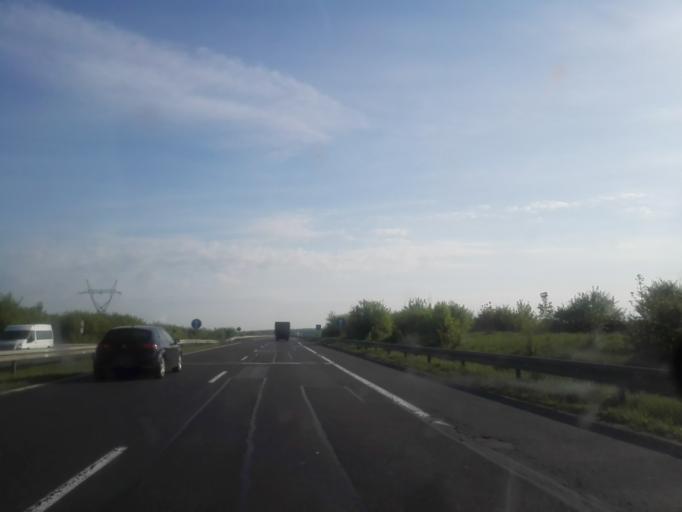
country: PL
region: Lodz Voivodeship
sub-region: Powiat piotrkowski
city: Wola Krzysztoporska
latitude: 51.2900
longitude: 19.5420
